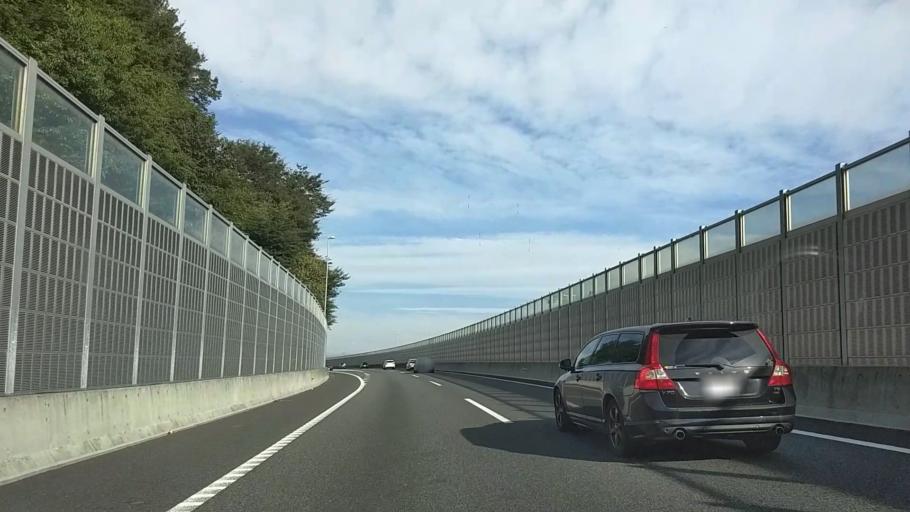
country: JP
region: Kanagawa
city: Zama
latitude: 35.5198
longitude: 139.3577
